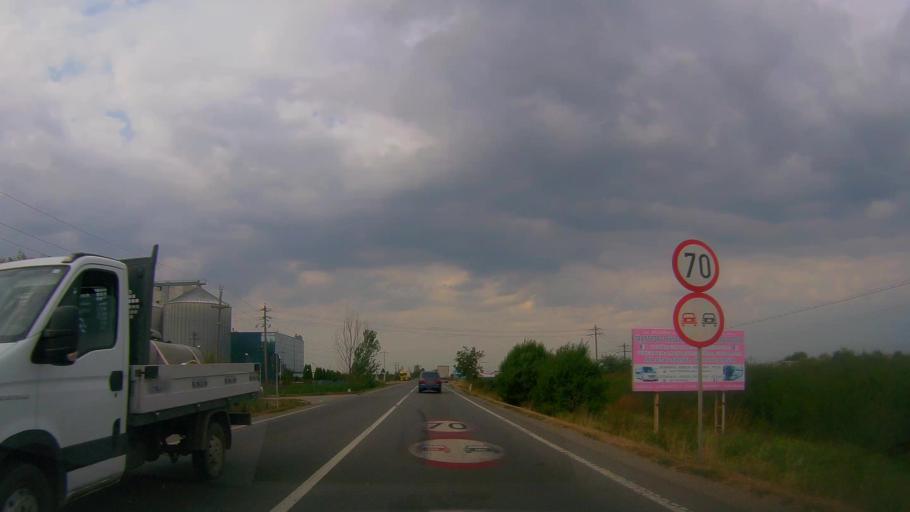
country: RO
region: Satu Mare
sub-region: Comuna Botiz
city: Botiz
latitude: 47.8218
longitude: 22.9397
